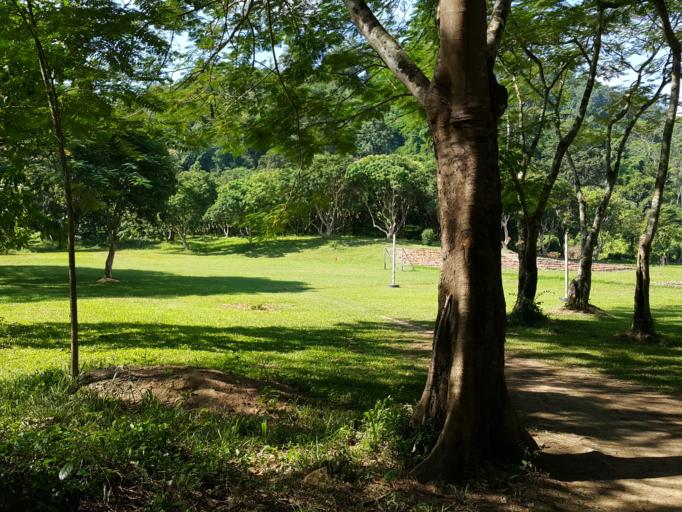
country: TH
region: Chiang Mai
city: Mae Taeng
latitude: 19.1973
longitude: 98.8850
